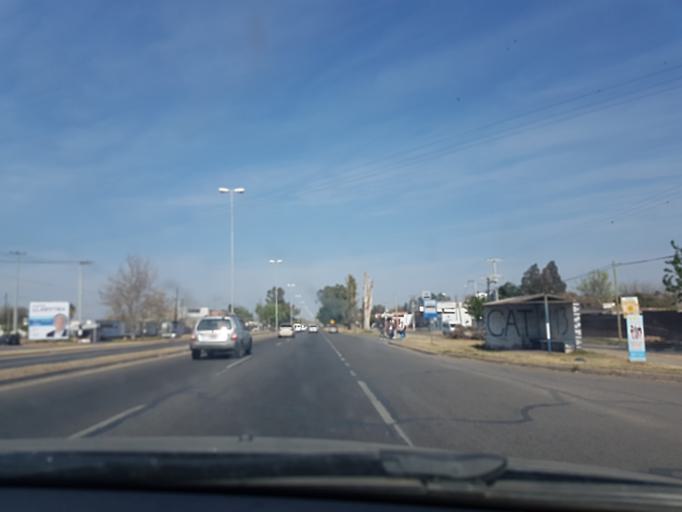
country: AR
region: Cordoba
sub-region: Departamento de Capital
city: Cordoba
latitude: -31.4729
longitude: -64.2314
